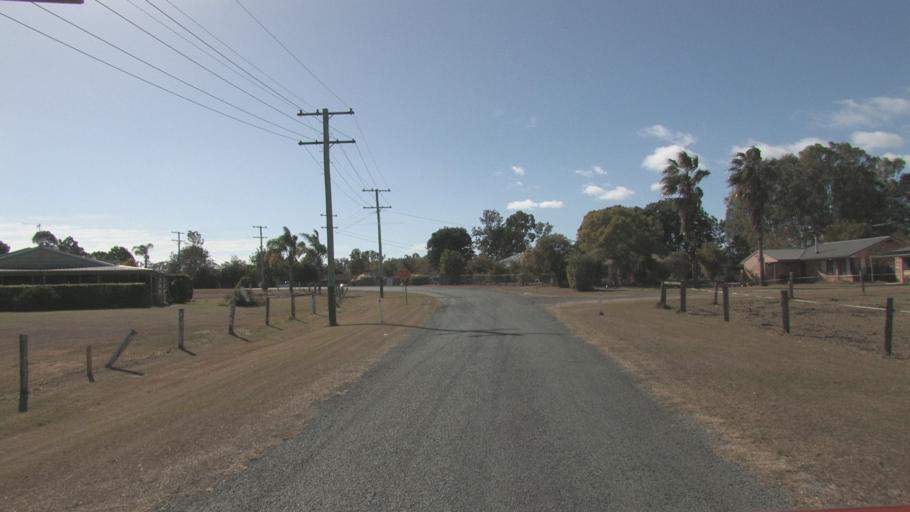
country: AU
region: Queensland
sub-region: Logan
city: Cedar Vale
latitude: -27.8531
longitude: 152.9773
